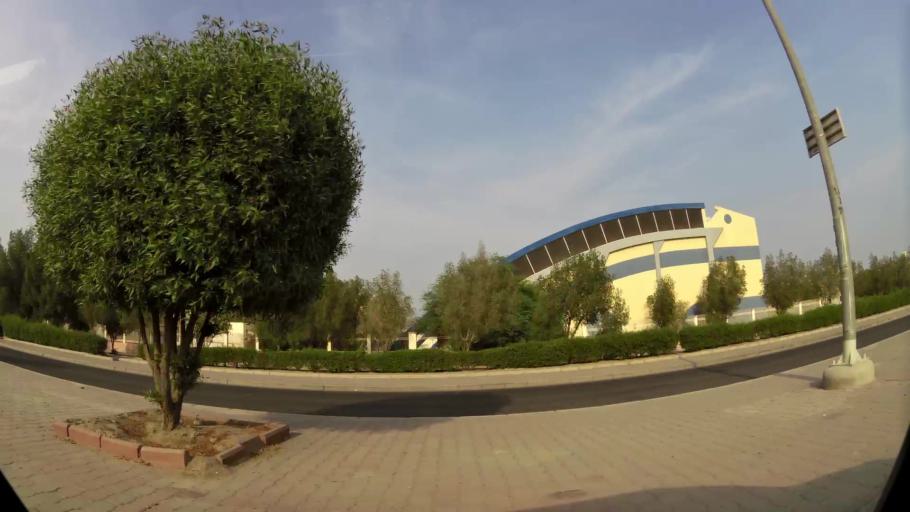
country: KW
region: Mubarak al Kabir
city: Sabah as Salim
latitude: 29.2465
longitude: 48.0558
